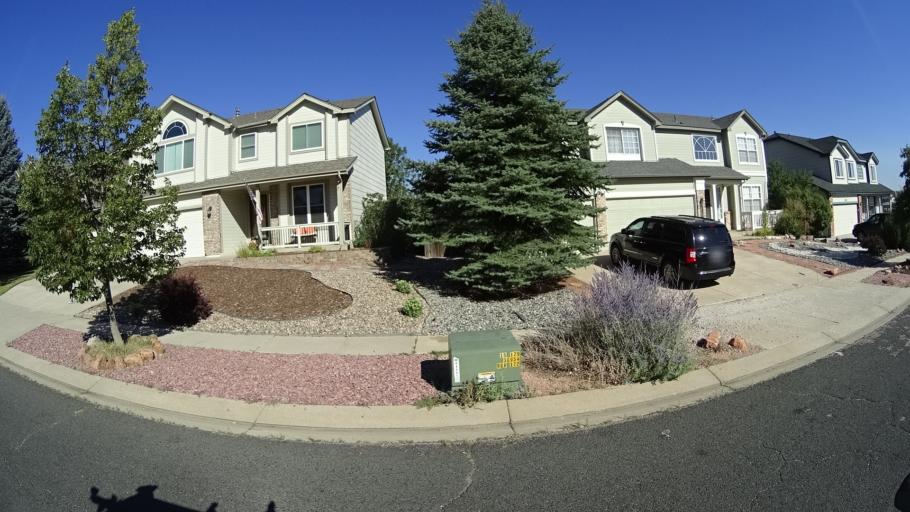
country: US
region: Colorado
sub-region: El Paso County
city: Black Forest
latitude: 38.9616
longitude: -104.7577
